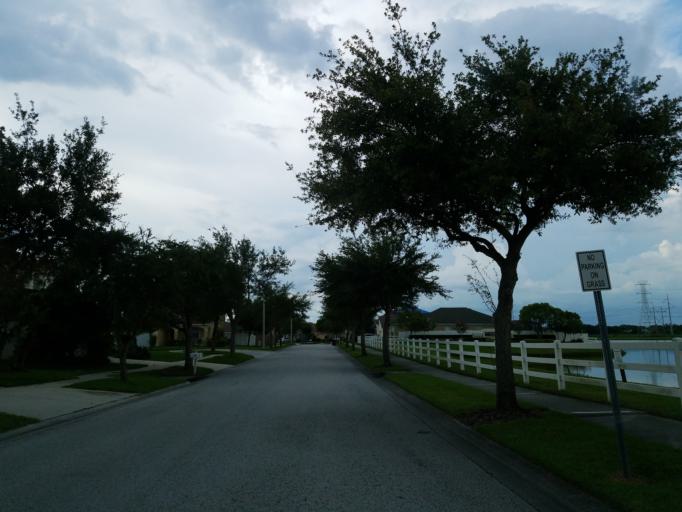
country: US
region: Florida
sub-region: Hillsborough County
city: Progress Village
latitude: 27.9091
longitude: -82.3631
